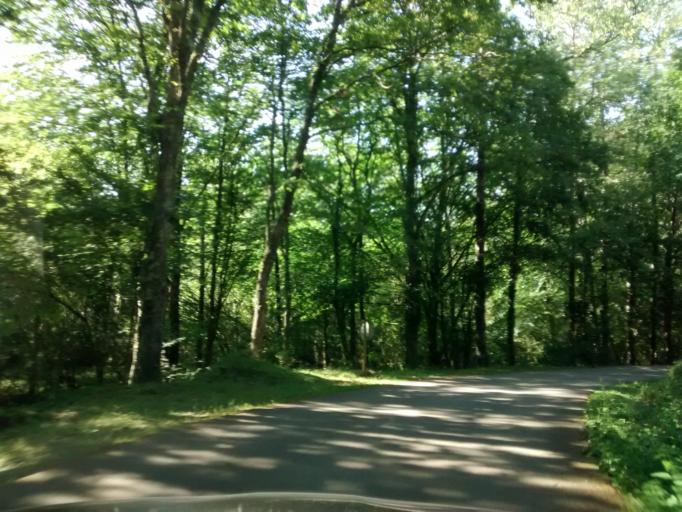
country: ES
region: Cantabria
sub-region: Provincia de Cantabria
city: Ruente
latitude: 43.2392
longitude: -4.2317
